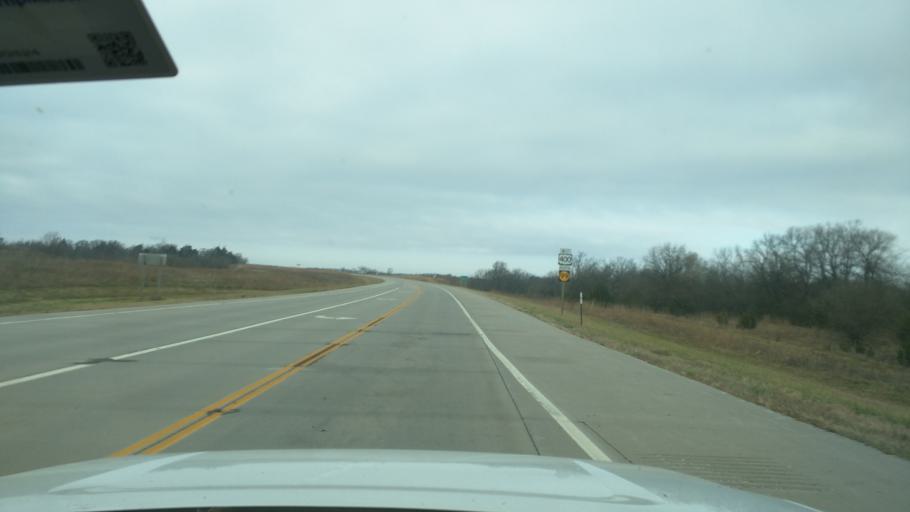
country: US
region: Kansas
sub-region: Elk County
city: Howard
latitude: 37.6369
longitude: -96.2350
